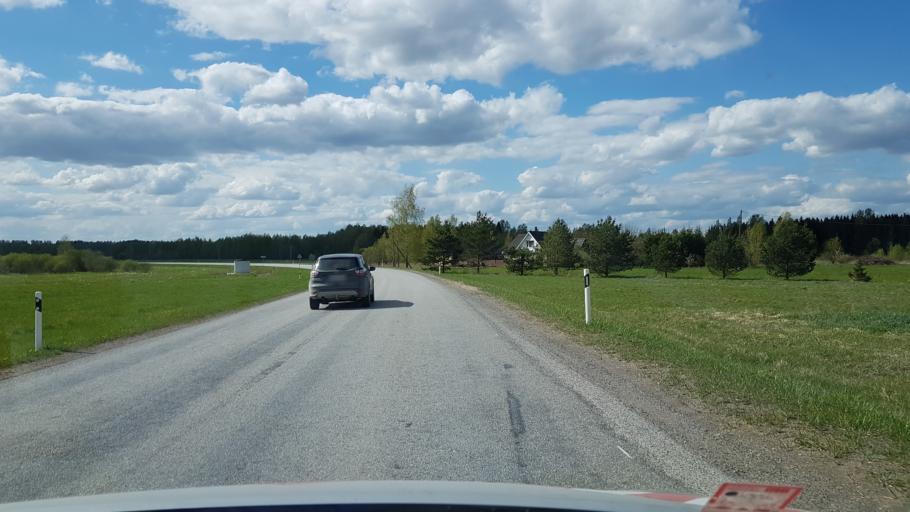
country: EE
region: Polvamaa
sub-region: Polva linn
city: Polva
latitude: 58.2857
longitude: 27.0381
